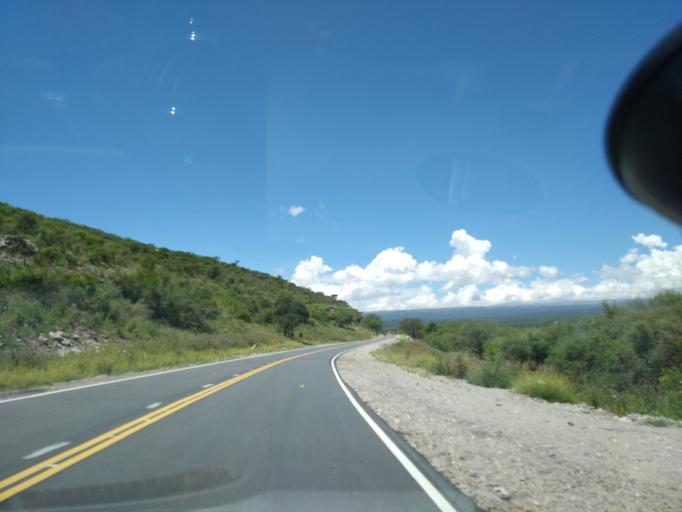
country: AR
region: Cordoba
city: Salsacate
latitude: -31.3457
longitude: -65.0990
